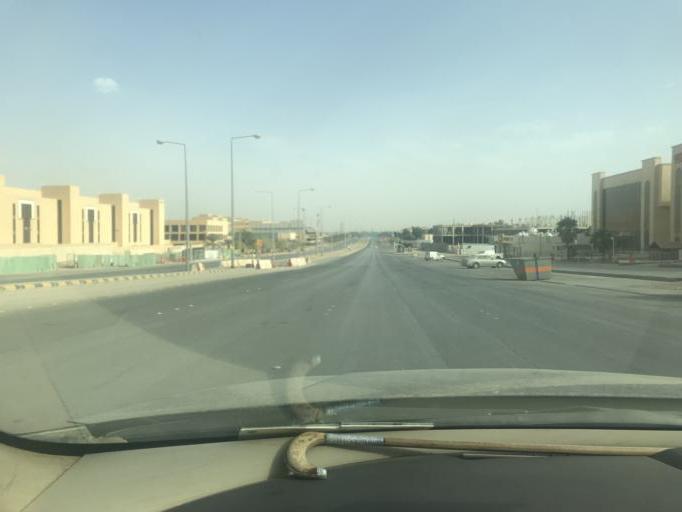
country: SA
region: Ar Riyad
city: Riyadh
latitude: 24.8152
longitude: 46.6889
